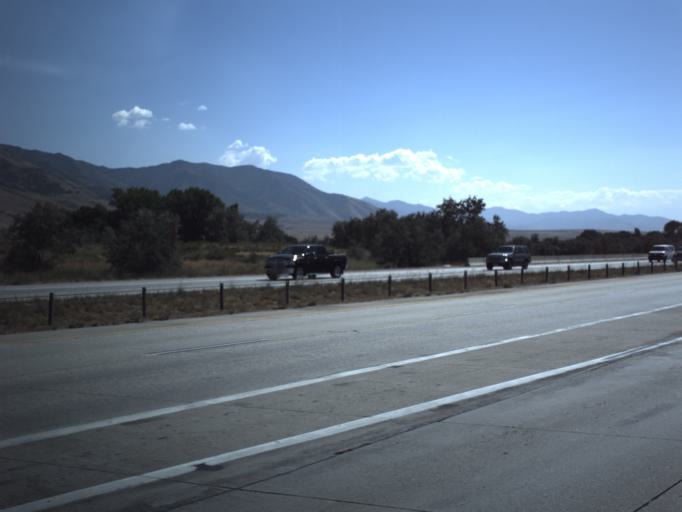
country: US
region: Utah
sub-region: Tooele County
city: Stansbury park
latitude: 40.7004
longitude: -112.2587
